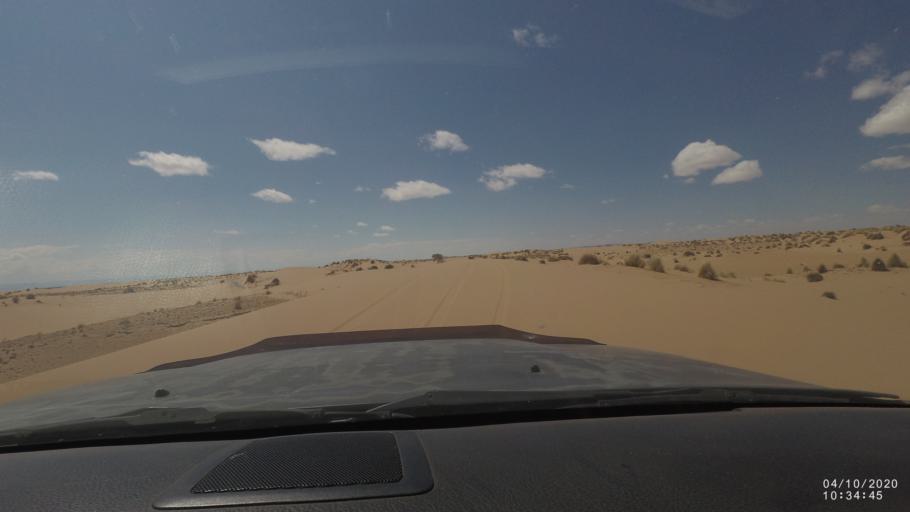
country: BO
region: Oruro
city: Poopo
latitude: -18.7047
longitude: -67.4771
